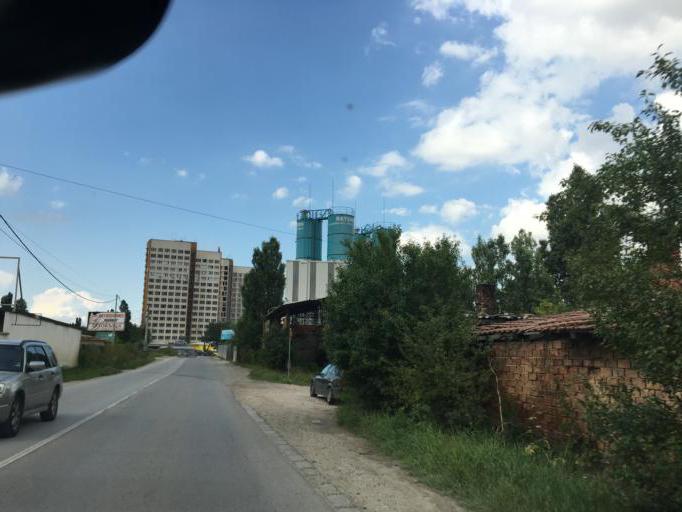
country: BG
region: Sofia-Capital
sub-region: Stolichna Obshtina
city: Sofia
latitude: 42.6446
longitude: 23.3536
